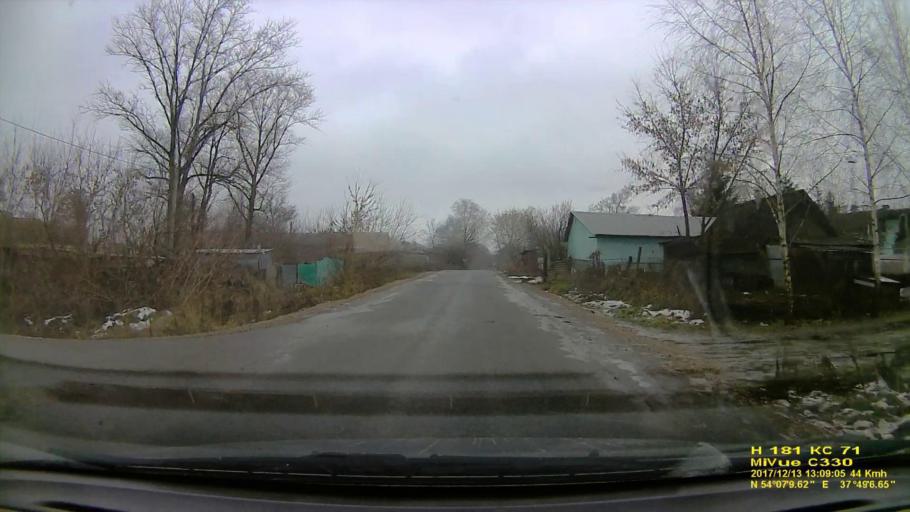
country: RU
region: Tula
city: Bolokhovo
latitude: 54.1193
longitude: 37.8188
